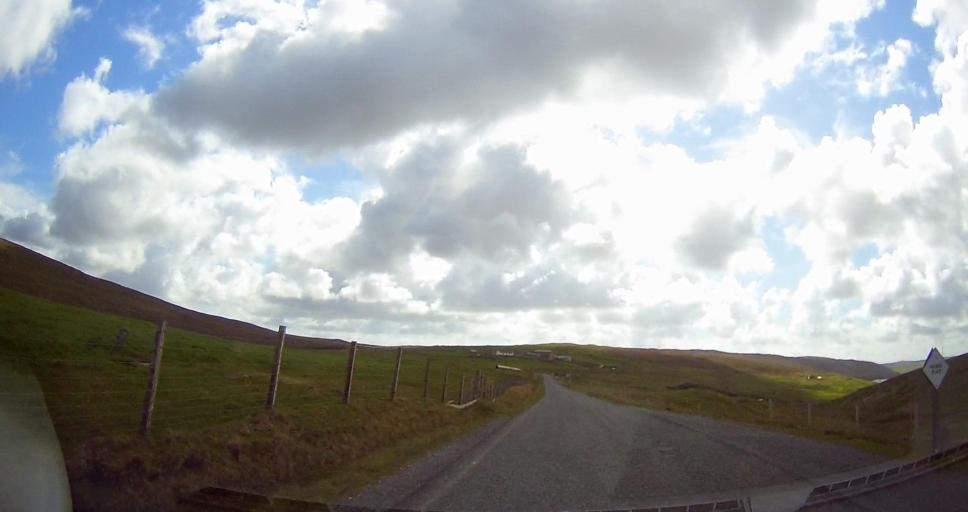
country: GB
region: Scotland
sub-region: Shetland Islands
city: Lerwick
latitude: 60.5143
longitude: -1.3825
